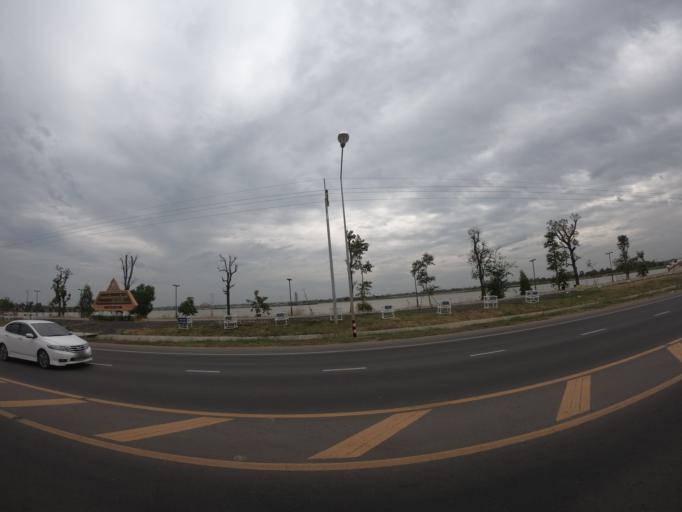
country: TH
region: Roi Et
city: Thawat Buri
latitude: 16.0828
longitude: 103.7192
